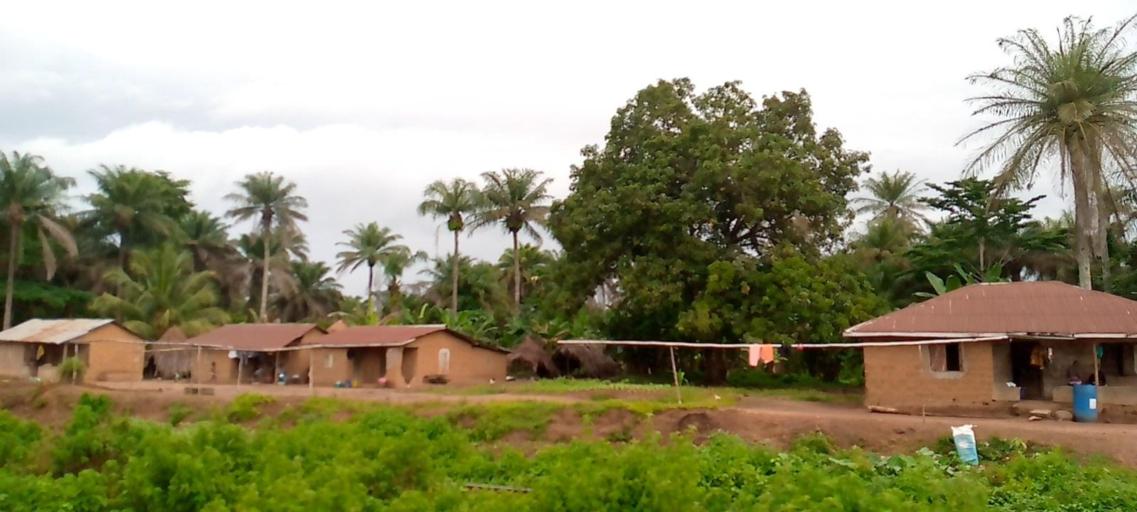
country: SL
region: Northern Province
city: Port Loko
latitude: 8.7204
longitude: -12.7880
